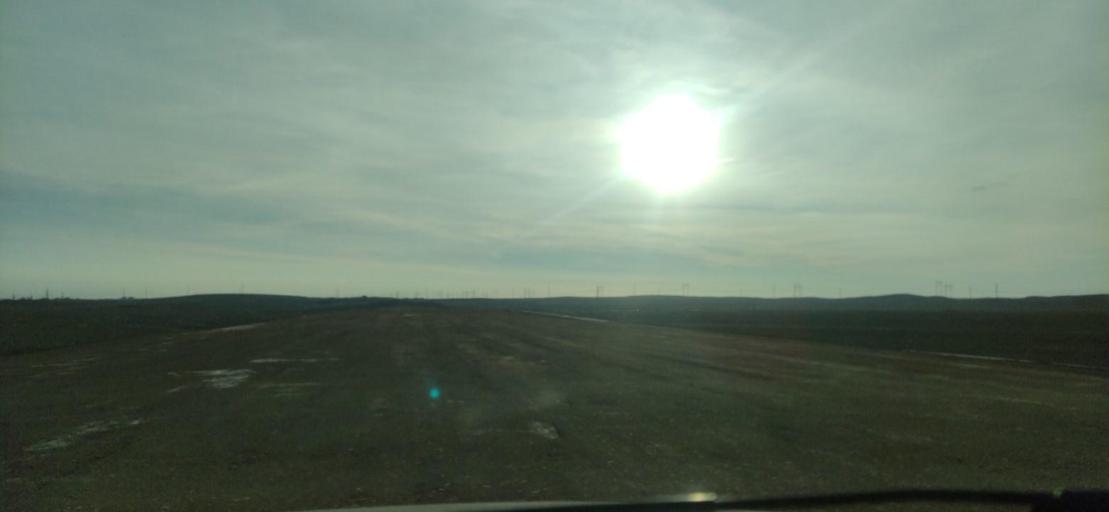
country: KZ
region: Qaraghandy
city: Saryshaghan
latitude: 46.1363
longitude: 73.6036
